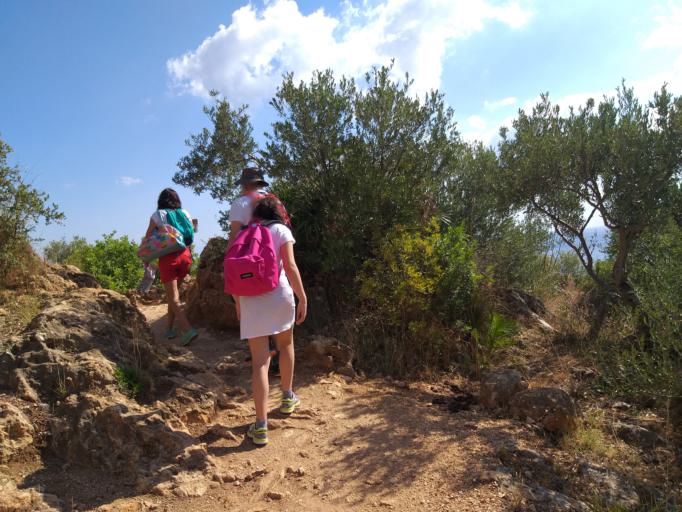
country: IT
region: Sicily
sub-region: Trapani
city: Castelluzzo
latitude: 38.0845
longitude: 12.8075
